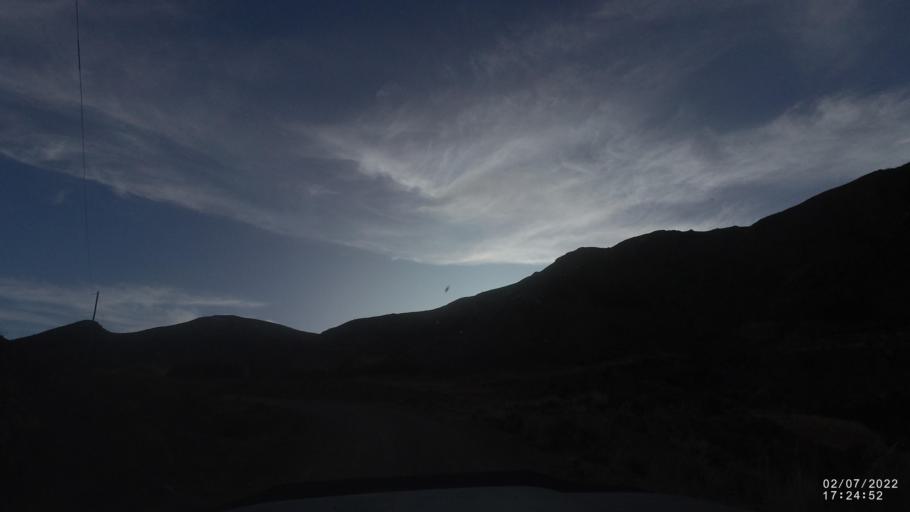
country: BO
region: Cochabamba
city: Irpa Irpa
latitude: -17.8747
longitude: -66.6056
